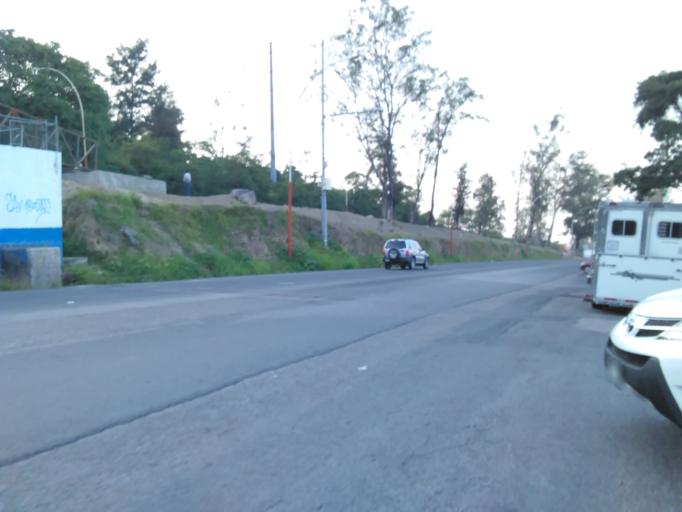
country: MX
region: Nayarit
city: Tepic
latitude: 21.5118
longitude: -104.9235
